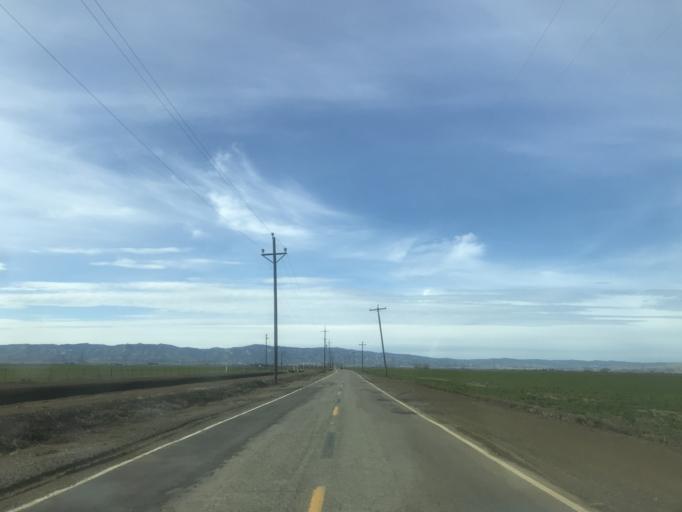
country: US
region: California
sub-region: Yolo County
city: Cottonwood
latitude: 38.6637
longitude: -121.9132
